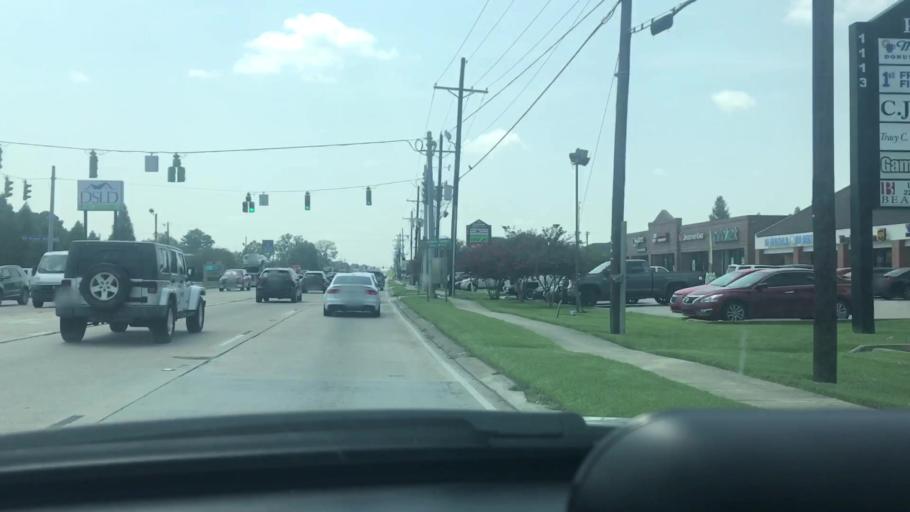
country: US
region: Louisiana
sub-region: Livingston Parish
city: Denham Springs
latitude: 30.4704
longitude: -90.9567
